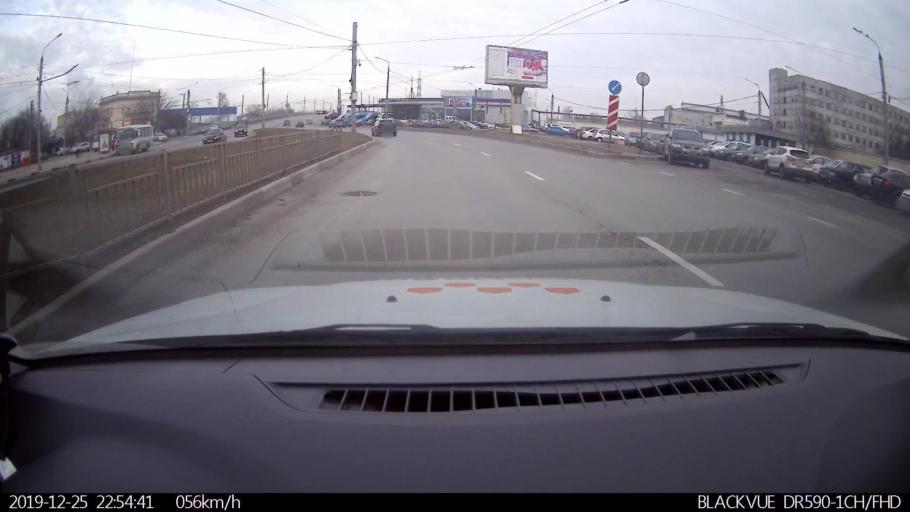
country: RU
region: Nizjnij Novgorod
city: Nizhniy Novgorod
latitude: 56.2573
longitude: 43.9028
